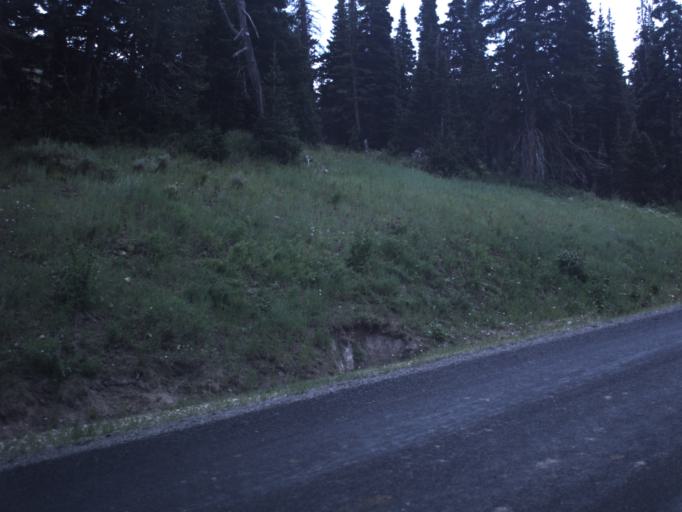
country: US
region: Utah
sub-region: Summit County
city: Francis
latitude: 40.4865
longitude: -111.0339
